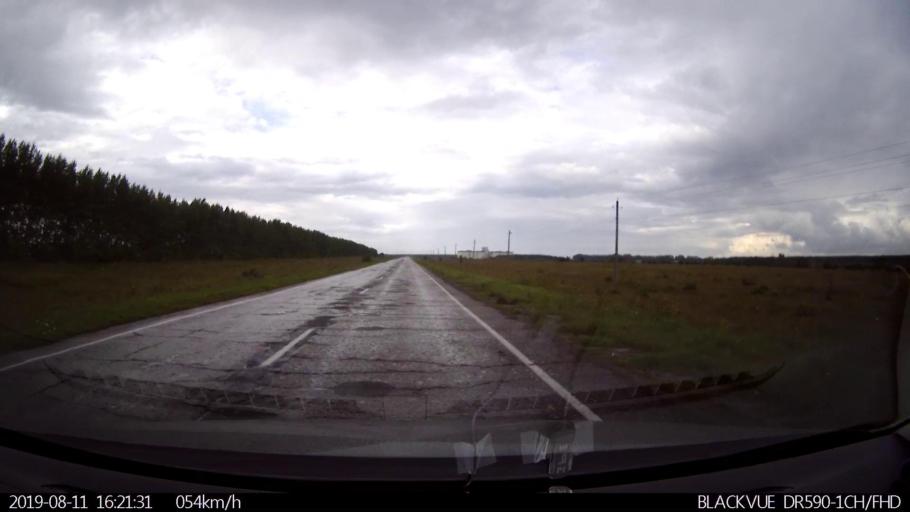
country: RU
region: Ulyanovsk
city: Mayna
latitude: 54.0804
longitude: 47.5976
